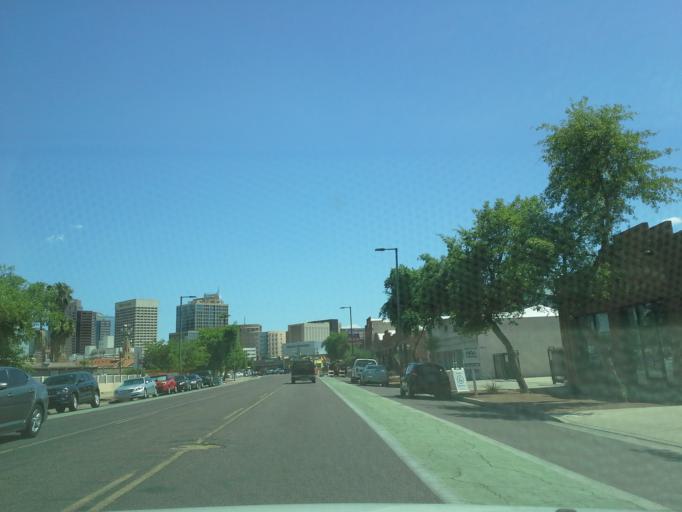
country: US
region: Arizona
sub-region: Maricopa County
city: Phoenix
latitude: 33.4530
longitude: -112.0845
